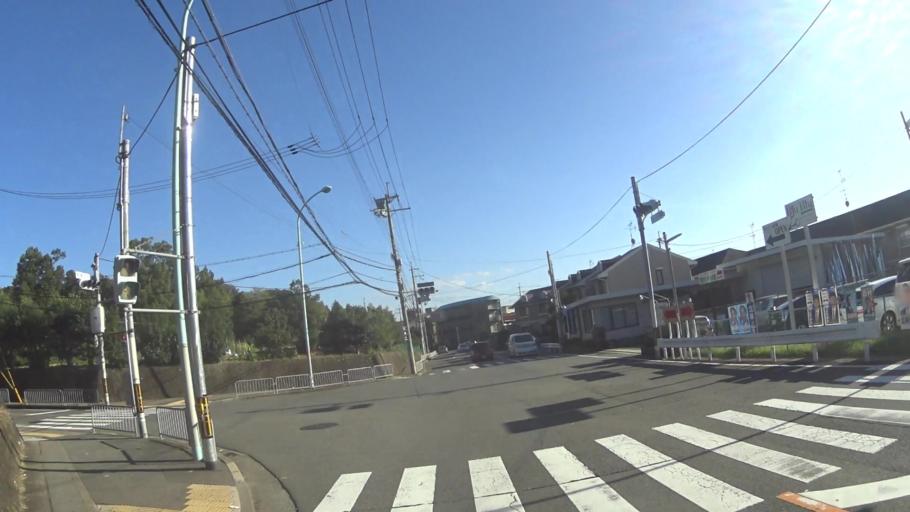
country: JP
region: Kyoto
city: Muko
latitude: 34.9686
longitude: 135.6793
